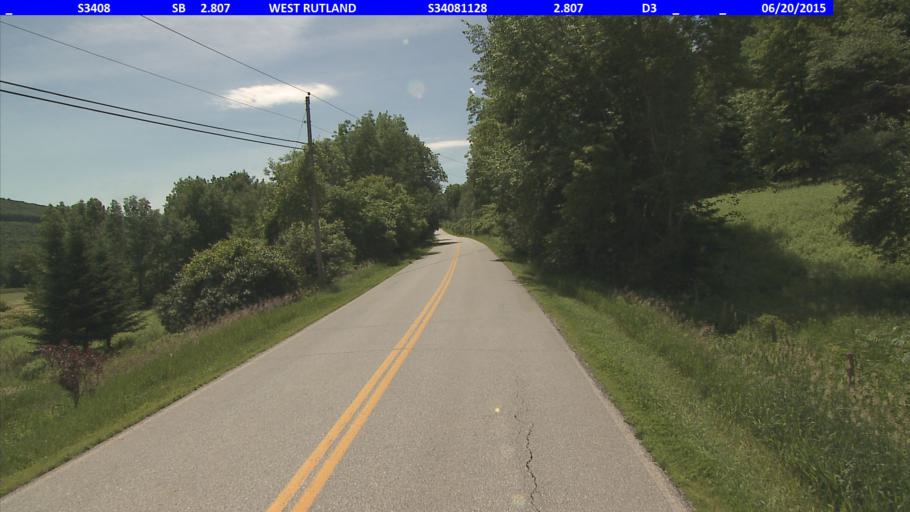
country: US
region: Vermont
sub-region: Rutland County
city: West Rutland
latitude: 43.6493
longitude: -73.0729
